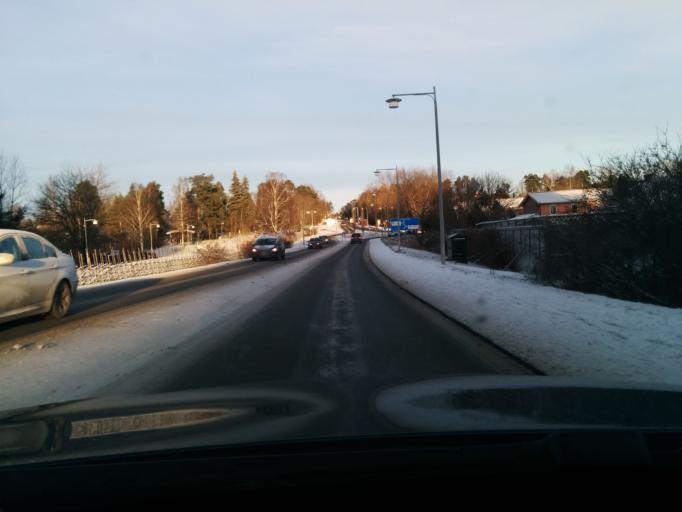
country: SE
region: Stockholm
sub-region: Vallentuna Kommun
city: Vallentuna
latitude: 59.4977
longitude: 18.0625
